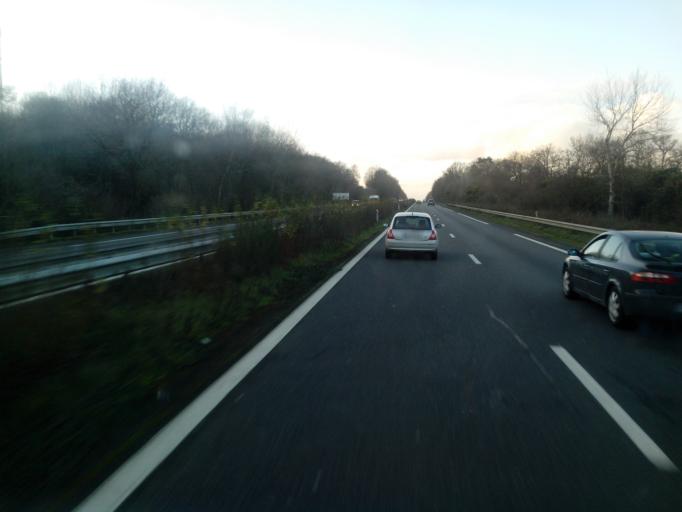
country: FR
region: Pays de la Loire
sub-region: Departement de la Loire-Atlantique
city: Haute-Goulaine
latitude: 47.1871
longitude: -1.4238
